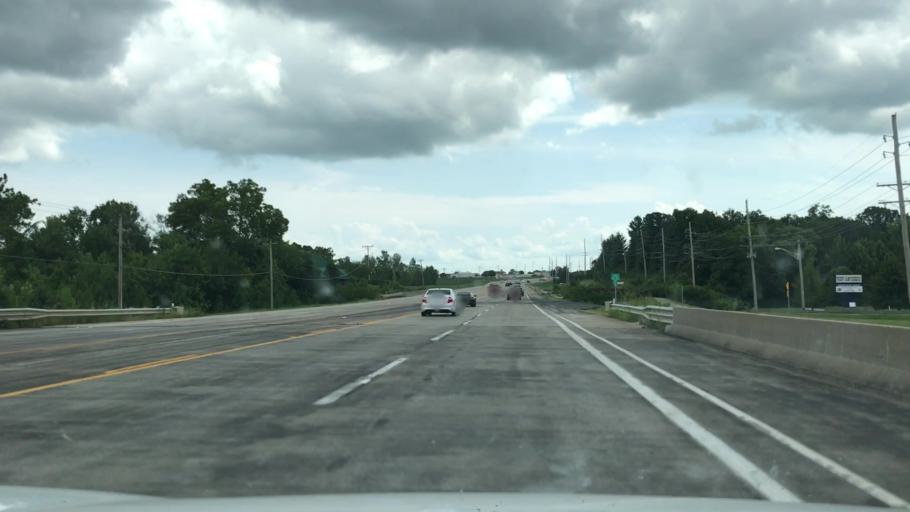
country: US
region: Missouri
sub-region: Saint Charles County
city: Weldon Spring
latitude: 38.7404
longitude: -90.6950
